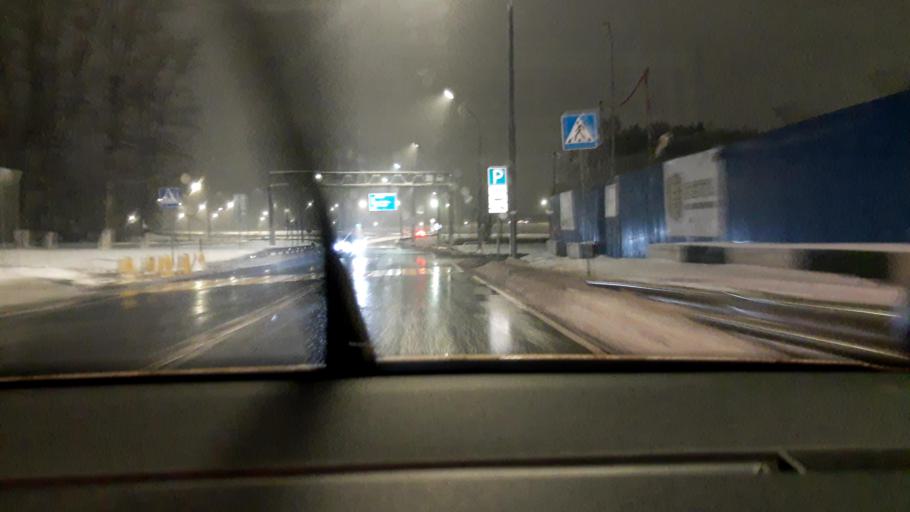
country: RU
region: Moskovskaya
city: Vostryakovo
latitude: 55.4308
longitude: 37.8739
